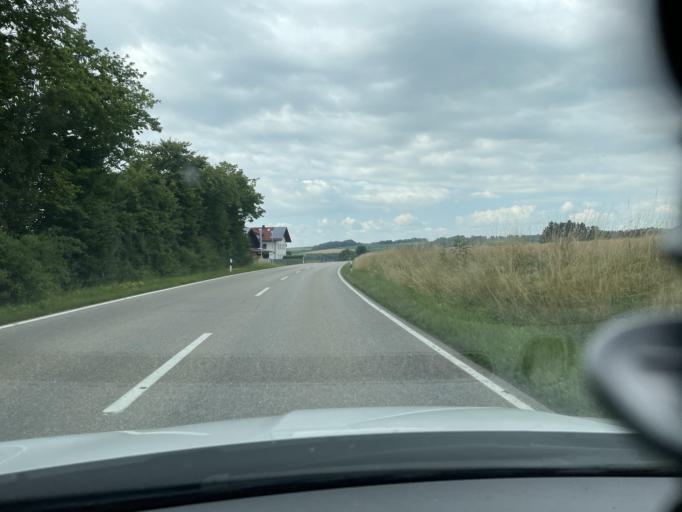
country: DE
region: Bavaria
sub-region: Upper Bavaria
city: Sankt Wolfgang
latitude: 48.1938
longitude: 12.1458
